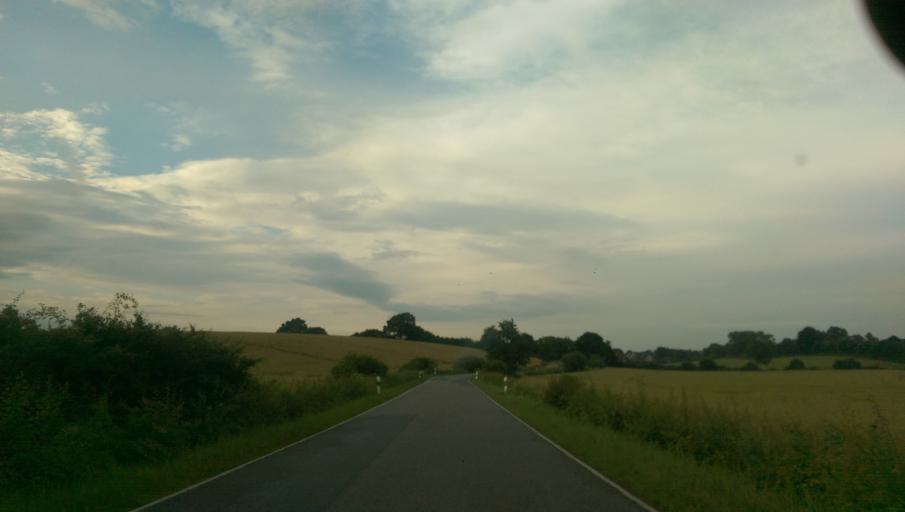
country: DE
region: Schleswig-Holstein
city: Barnitz
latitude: 53.7979
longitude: 10.4932
